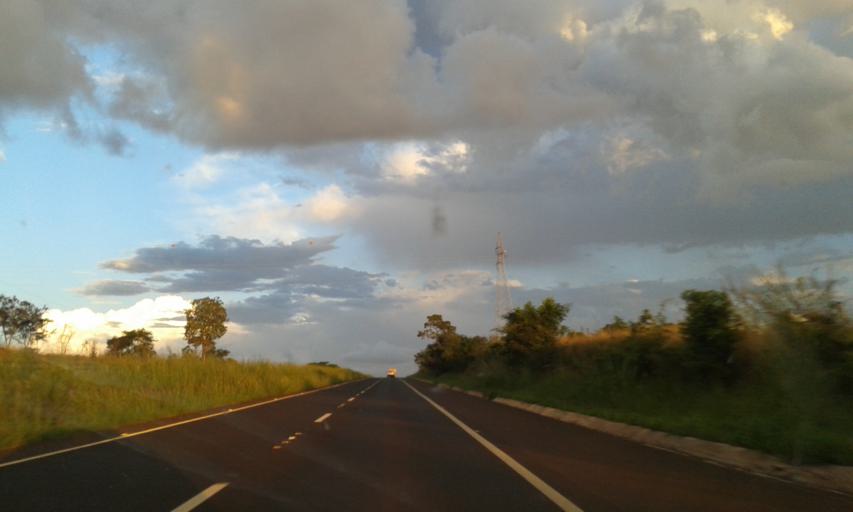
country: BR
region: Minas Gerais
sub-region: Monte Alegre De Minas
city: Monte Alegre de Minas
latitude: -18.8778
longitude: -48.7455
